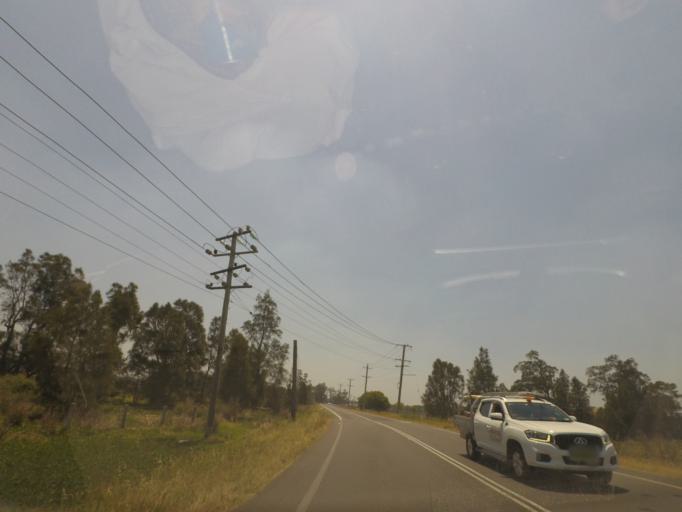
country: AU
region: New South Wales
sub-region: Port Stephens Shire
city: Medowie
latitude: -32.8010
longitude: 151.8888
